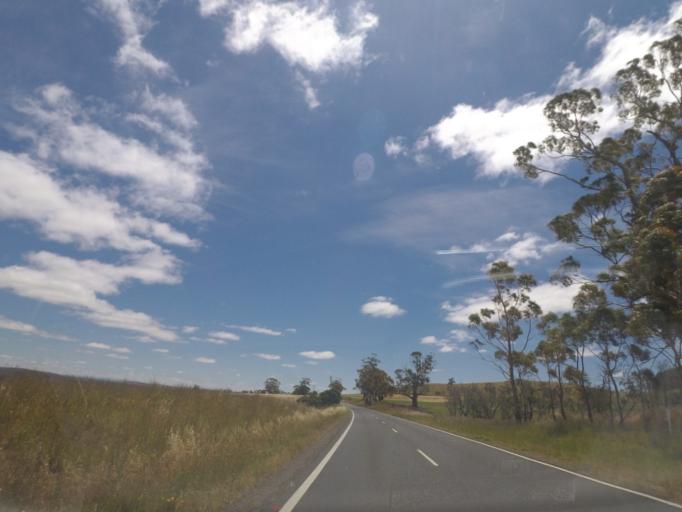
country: AU
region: Victoria
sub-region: Mount Alexander
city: Castlemaine
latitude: -37.2725
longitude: 144.1456
